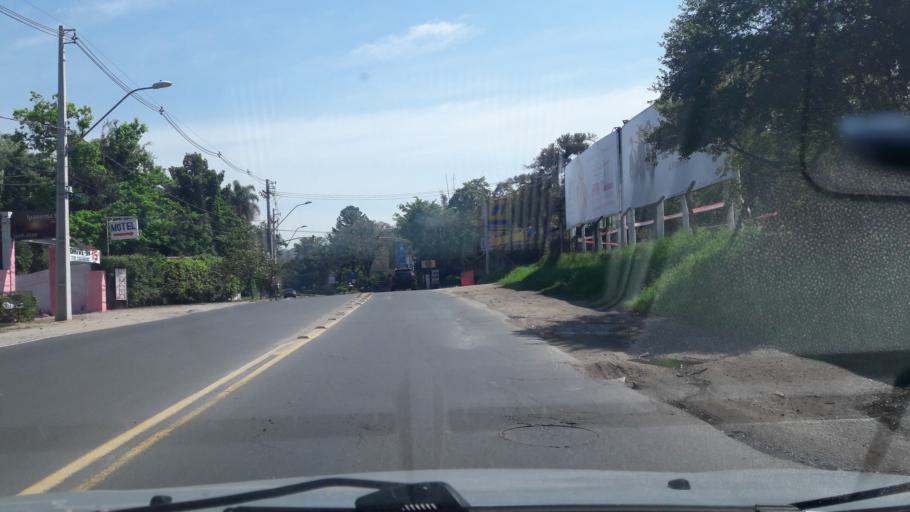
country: BR
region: Rio Grande do Sul
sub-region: Guaiba
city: Guaiba
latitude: -30.1247
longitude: -51.2448
